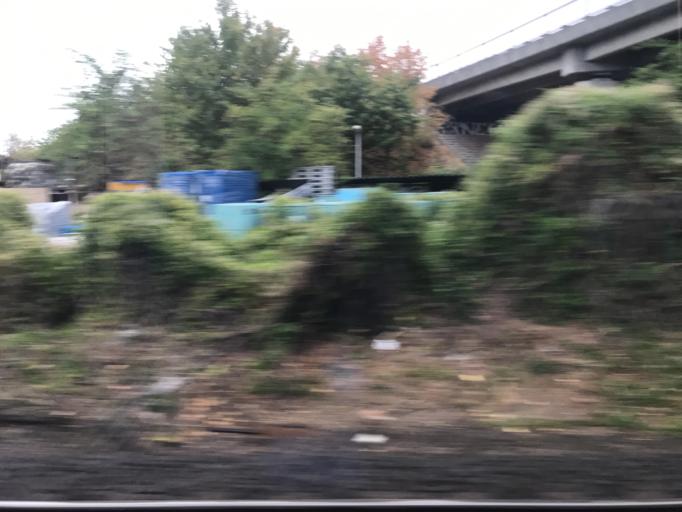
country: DE
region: Hesse
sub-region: Regierungsbezirk Darmstadt
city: Riedstadt
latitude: 49.8364
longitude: 8.4914
